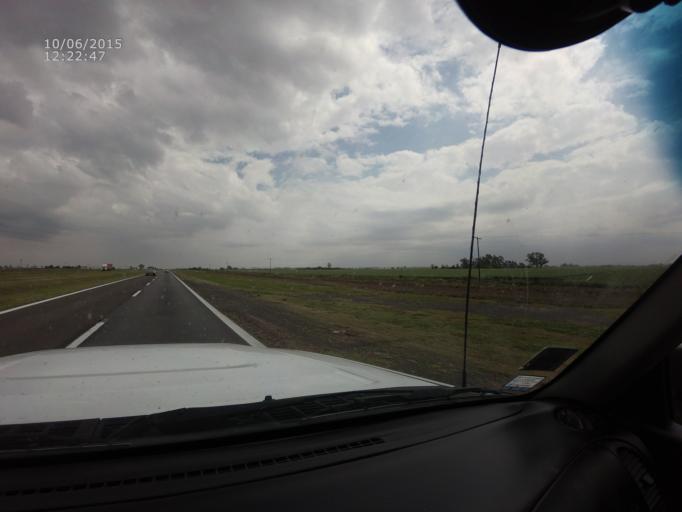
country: AR
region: Santa Fe
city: Roldan
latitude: -32.9166
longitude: -60.9437
